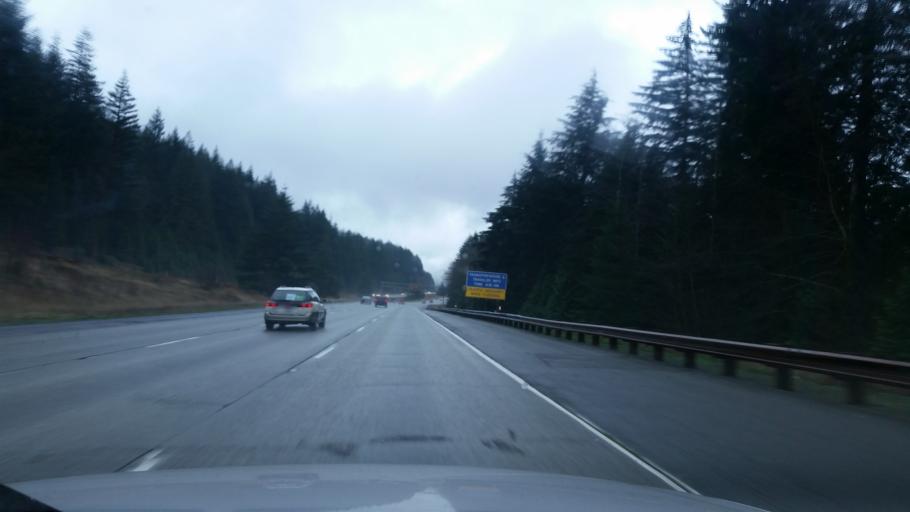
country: US
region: Washington
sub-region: King County
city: Tanner
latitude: 47.3976
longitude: -121.5473
